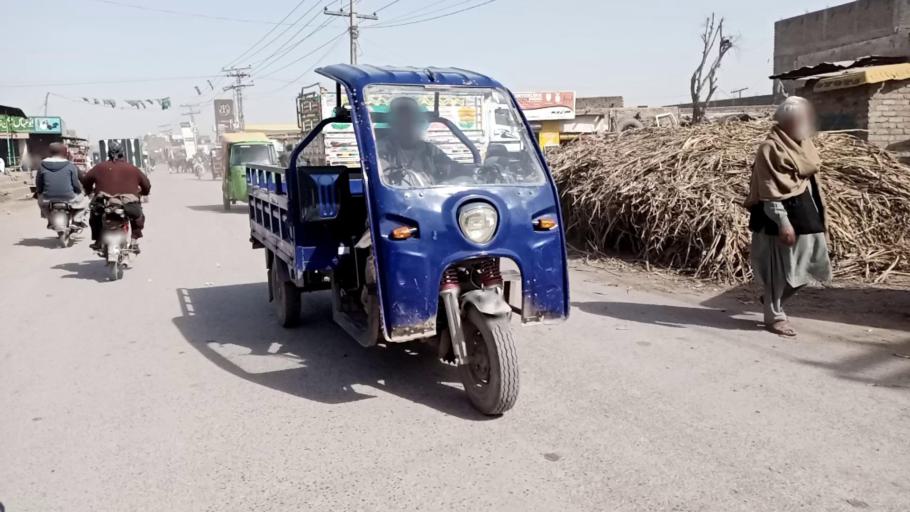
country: PK
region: Khyber Pakhtunkhwa
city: Peshawar
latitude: 33.9888
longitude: 71.6332
